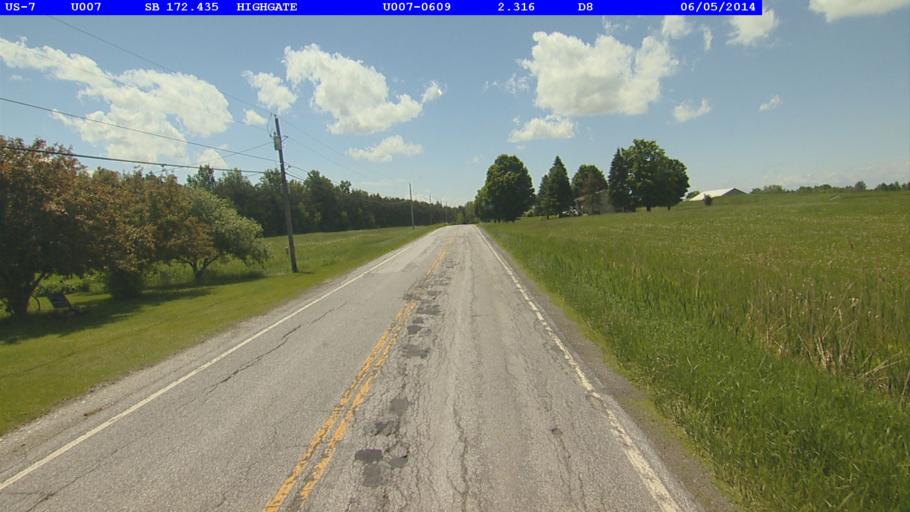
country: US
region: Vermont
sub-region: Franklin County
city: Swanton
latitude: 44.9657
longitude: -73.1085
